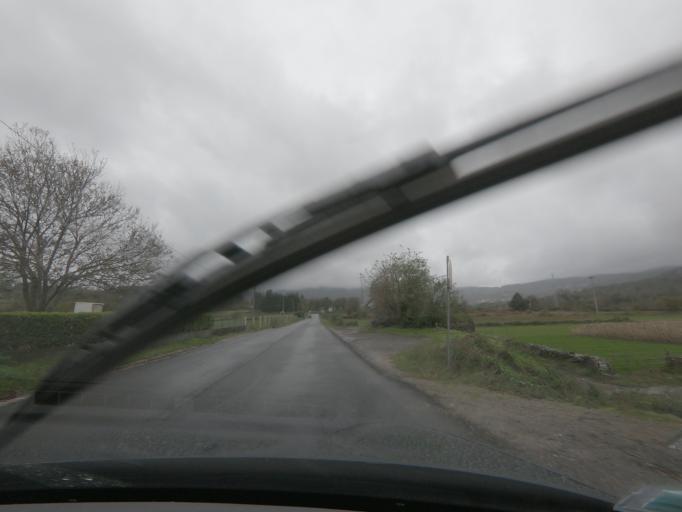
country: PT
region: Vila Real
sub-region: Santa Marta de Penaguiao
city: Santa Marta de Penaguiao
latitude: 41.2856
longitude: -7.8618
